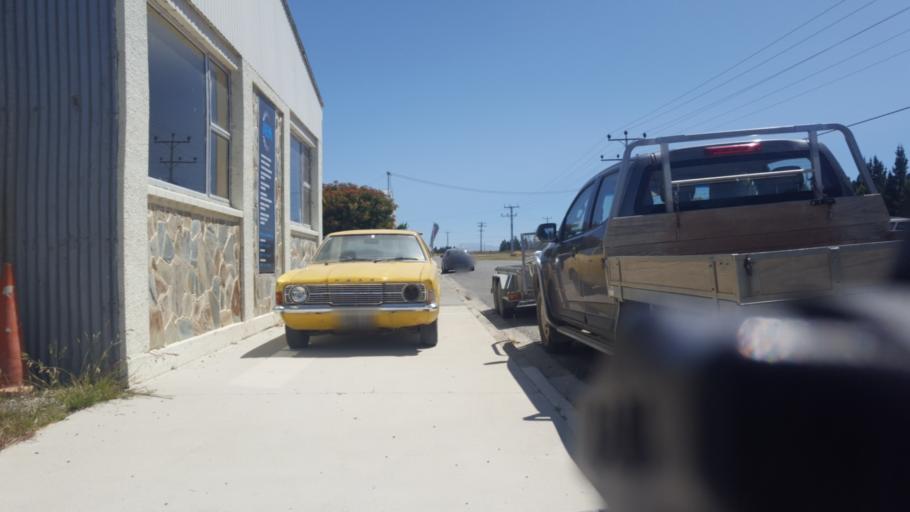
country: NZ
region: Otago
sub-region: Dunedin City
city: Dunedin
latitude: -45.1286
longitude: 170.0962
